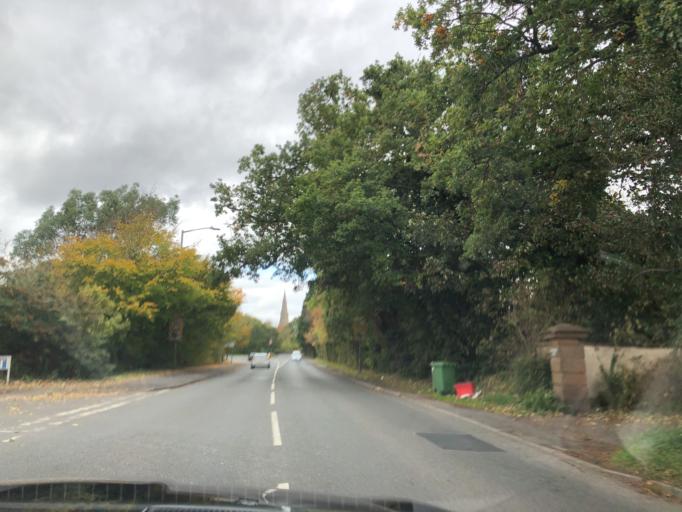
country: GB
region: England
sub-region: Warwickshire
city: Kenilworth
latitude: 52.3345
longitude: -1.5694
